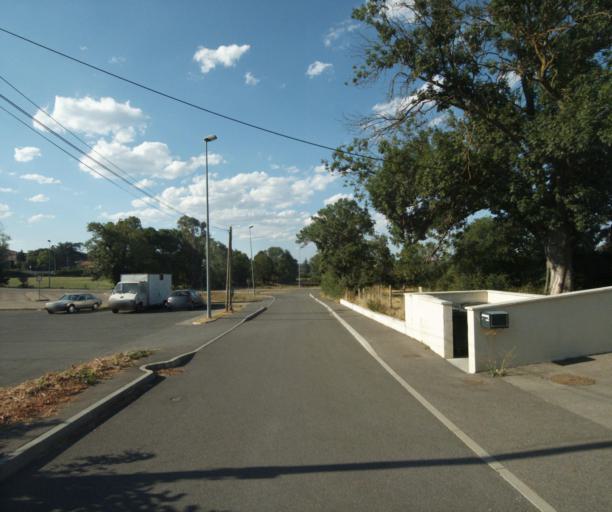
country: FR
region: Rhone-Alpes
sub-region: Departement du Rhone
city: Lentilly
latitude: 45.8162
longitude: 4.6668
